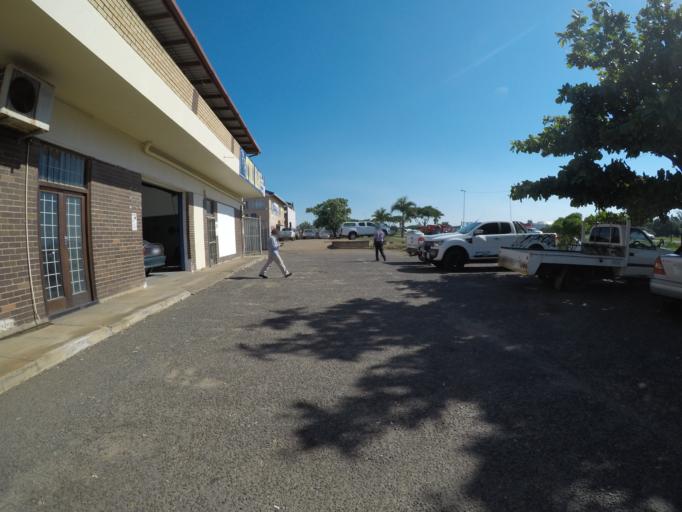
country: ZA
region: KwaZulu-Natal
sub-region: uThungulu District Municipality
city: Empangeni
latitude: -28.7720
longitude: 31.9025
